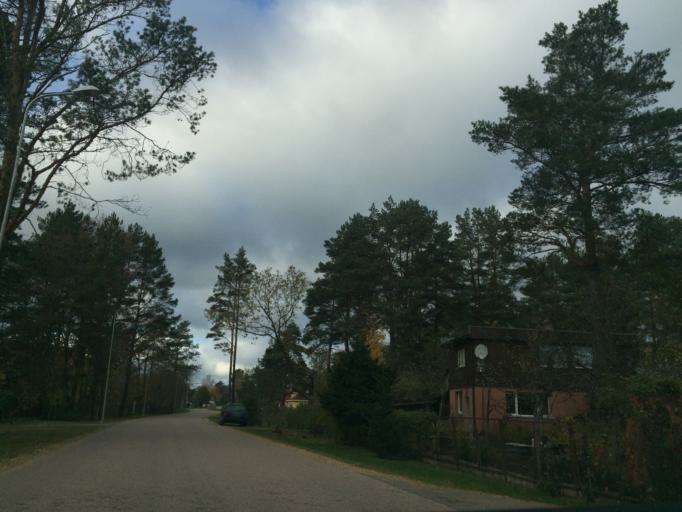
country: LV
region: Carnikava
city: Carnikava
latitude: 57.1276
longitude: 24.3119
